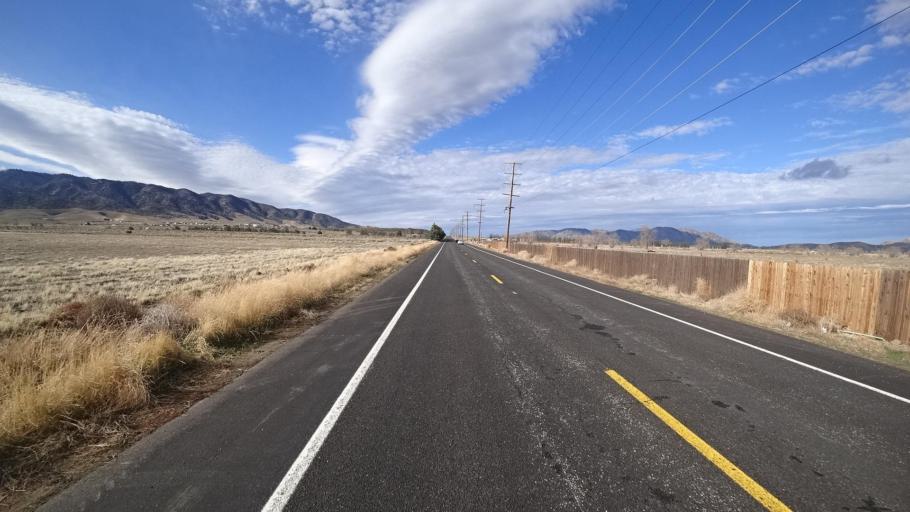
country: US
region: California
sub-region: Kern County
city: Tehachapi
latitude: 35.1082
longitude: -118.4293
